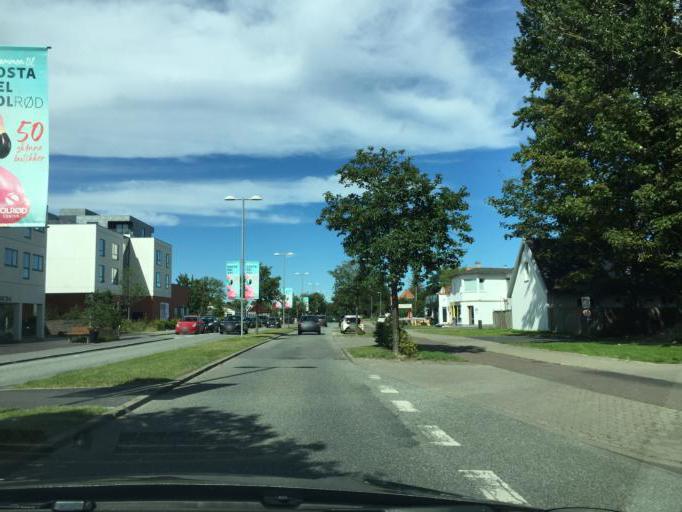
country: DK
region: Zealand
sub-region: Solrod Kommune
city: Solrod Strand
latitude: 55.5326
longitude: 12.2225
